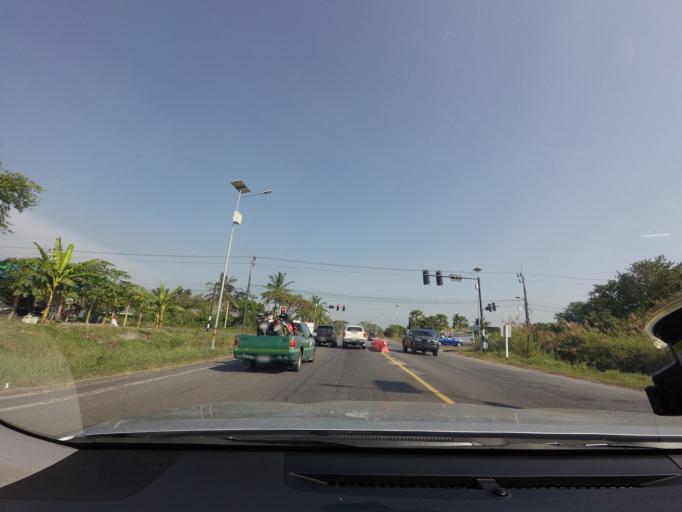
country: TH
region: Nakhon Si Thammarat
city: Nakhon Si Thammarat
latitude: 8.4761
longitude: 99.9788
